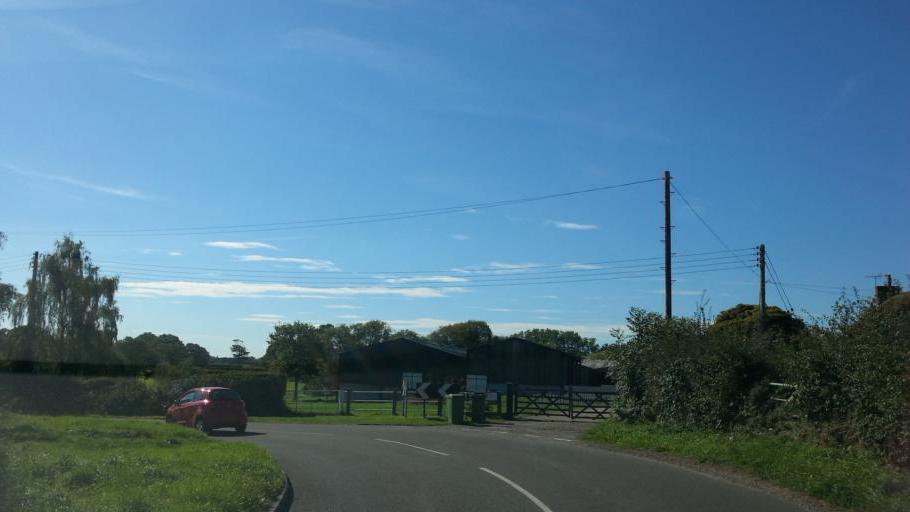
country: GB
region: England
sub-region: Staffordshire
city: Stafford
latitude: 52.8074
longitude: -2.1729
